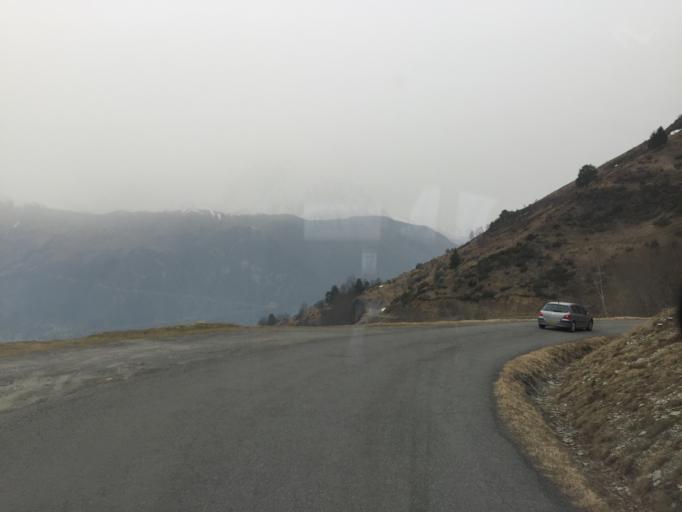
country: FR
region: Midi-Pyrenees
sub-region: Departement des Hautes-Pyrenees
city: Saint-Lary-Soulan
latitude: 42.8124
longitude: 0.3571
